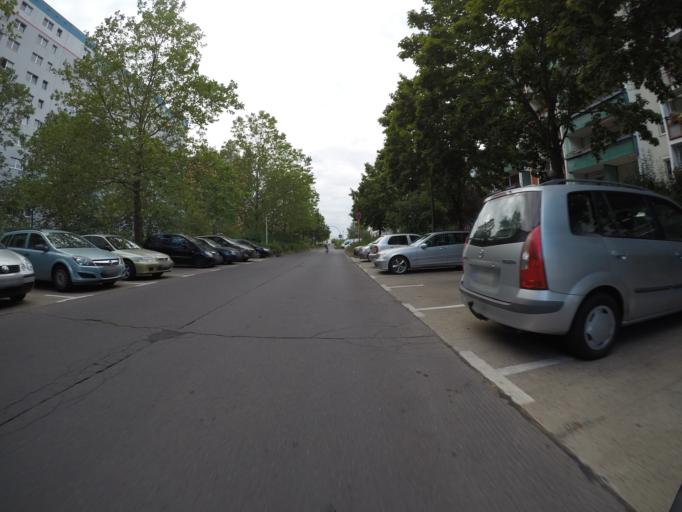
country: DE
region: Berlin
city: Kaulsdorf
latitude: 52.5229
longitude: 13.5922
